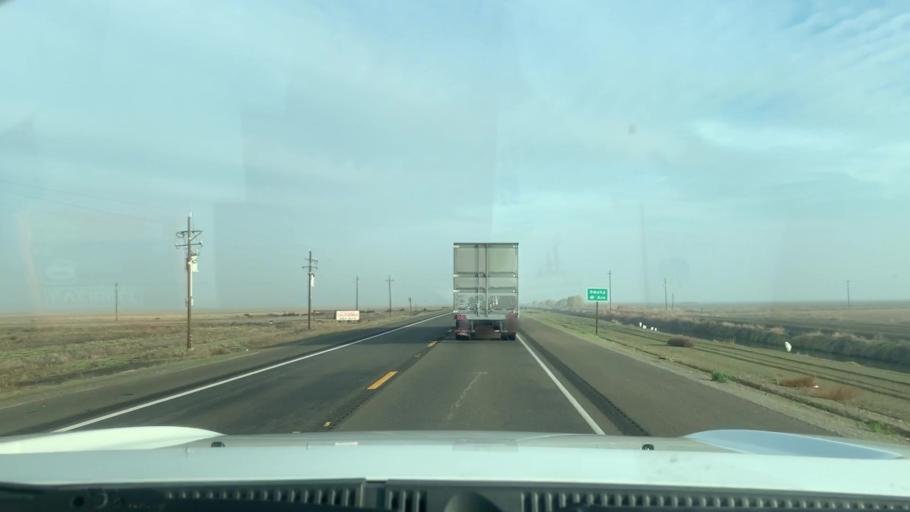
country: US
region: California
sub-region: Kings County
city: Kettleman City
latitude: 36.0923
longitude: -119.9116
